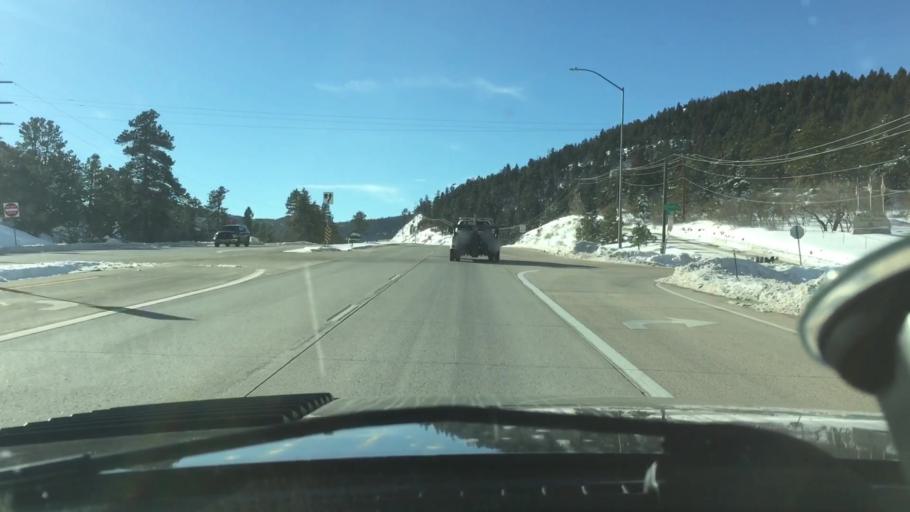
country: US
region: Colorado
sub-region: Jefferson County
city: Indian Hills
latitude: 39.5639
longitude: -105.2392
